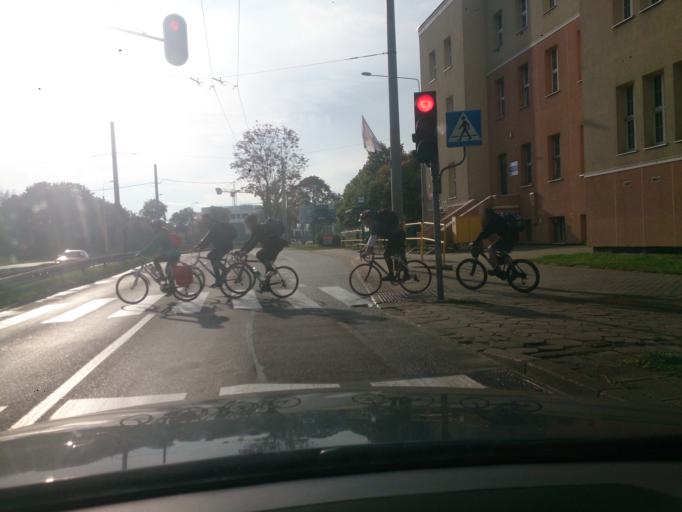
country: PL
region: Pomeranian Voivodeship
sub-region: Gdynia
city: Gdynia
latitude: 54.4827
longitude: 18.5493
